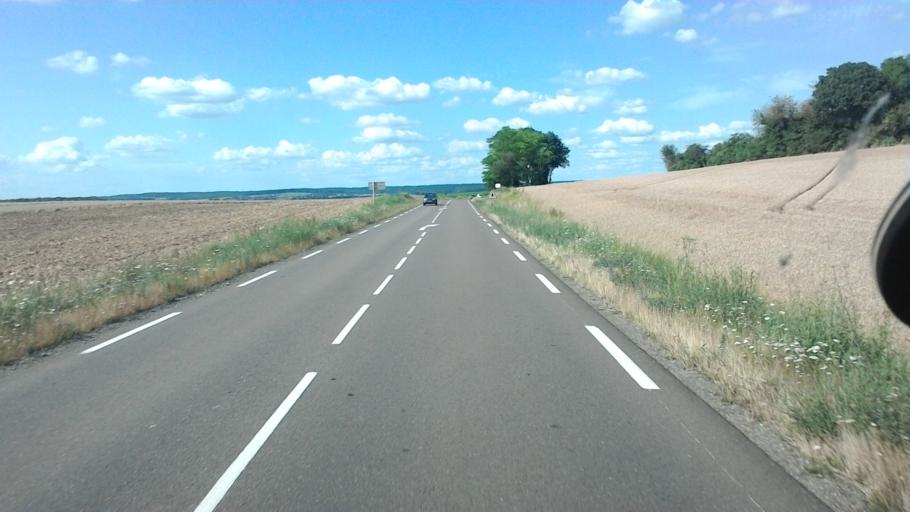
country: FR
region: Franche-Comte
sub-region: Departement de la Haute-Saone
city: Gy
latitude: 47.3909
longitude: 5.7903
